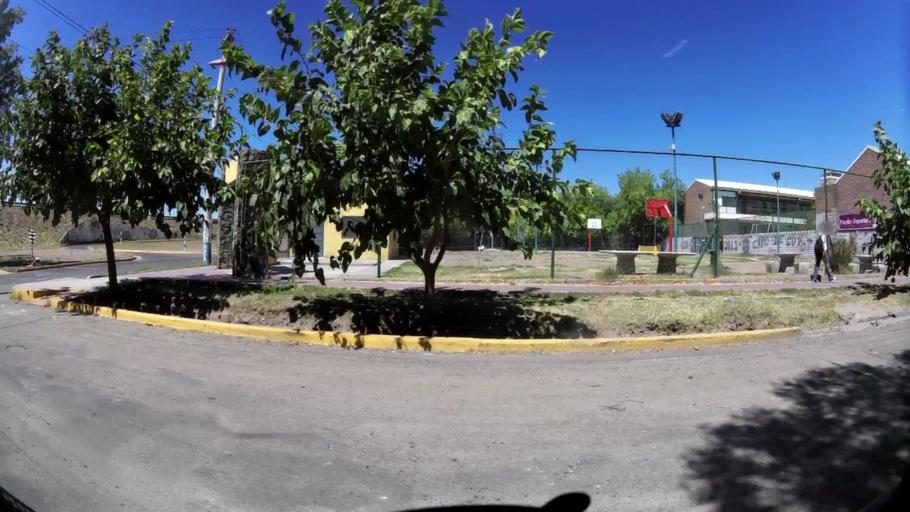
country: AR
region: Mendoza
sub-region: Departamento de Godoy Cruz
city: Godoy Cruz
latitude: -32.9323
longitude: -68.8645
